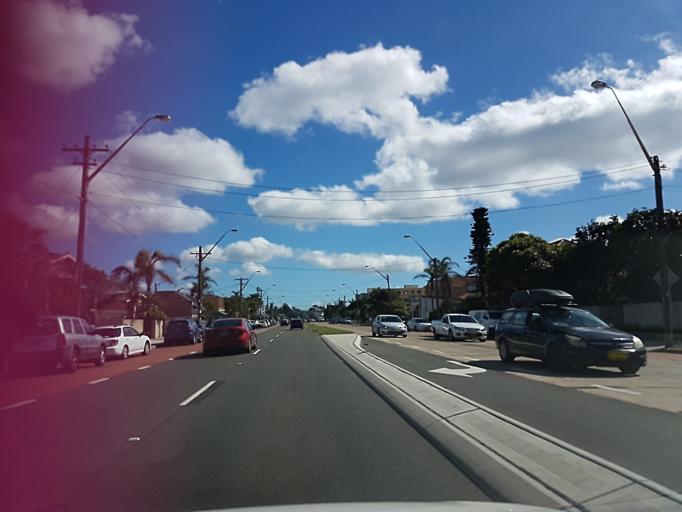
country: AU
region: New South Wales
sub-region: Warringah
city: Narrabeen
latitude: -33.7243
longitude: 151.2988
